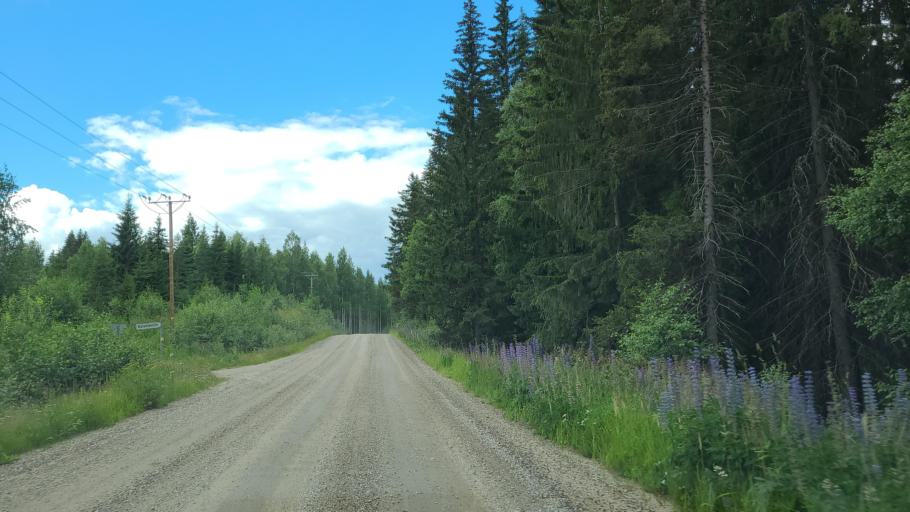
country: FI
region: Northern Savo
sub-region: Koillis-Savo
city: Kaavi
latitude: 62.9881
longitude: 28.5230
